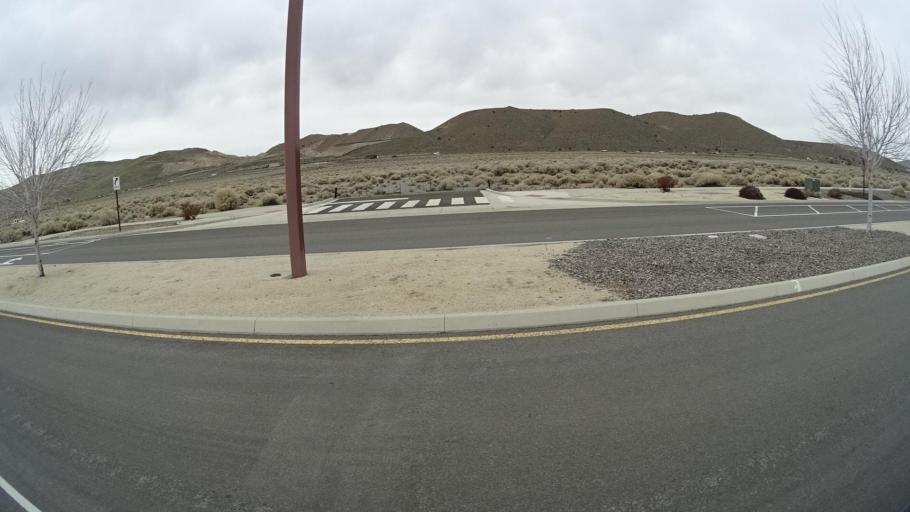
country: US
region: Nevada
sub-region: Washoe County
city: Spanish Springs
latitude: 39.6105
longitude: -119.7260
